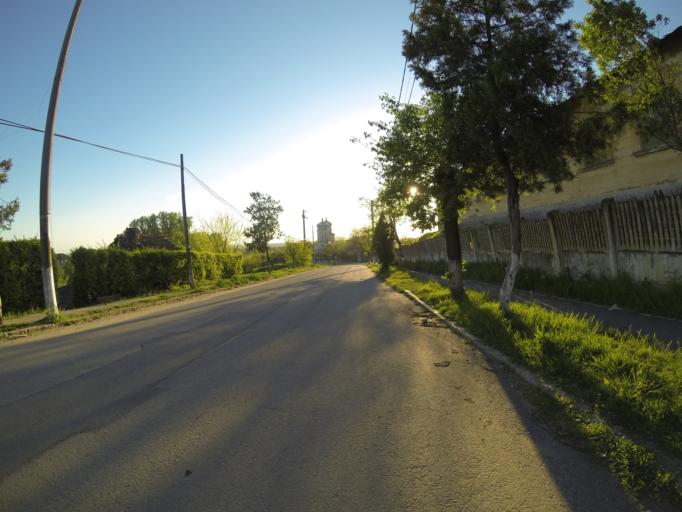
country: RO
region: Dolj
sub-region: Comuna Segarcea
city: Segarcea
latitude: 44.0957
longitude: 23.7444
